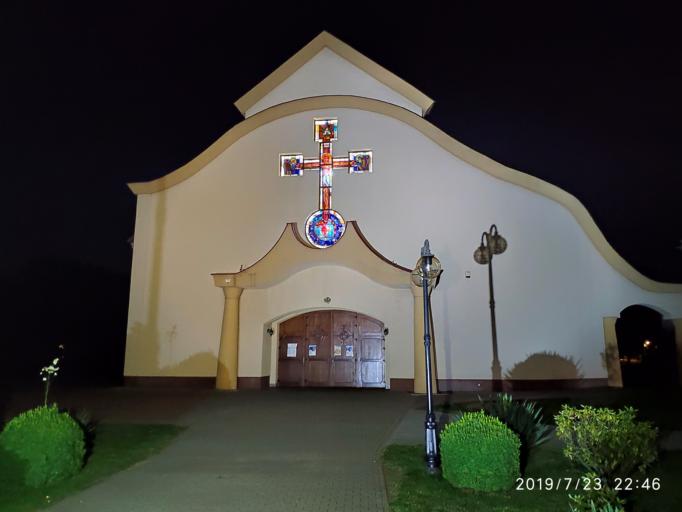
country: PL
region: Lubusz
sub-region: Zielona Gora
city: Zielona Gora
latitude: 51.9559
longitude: 15.4990
